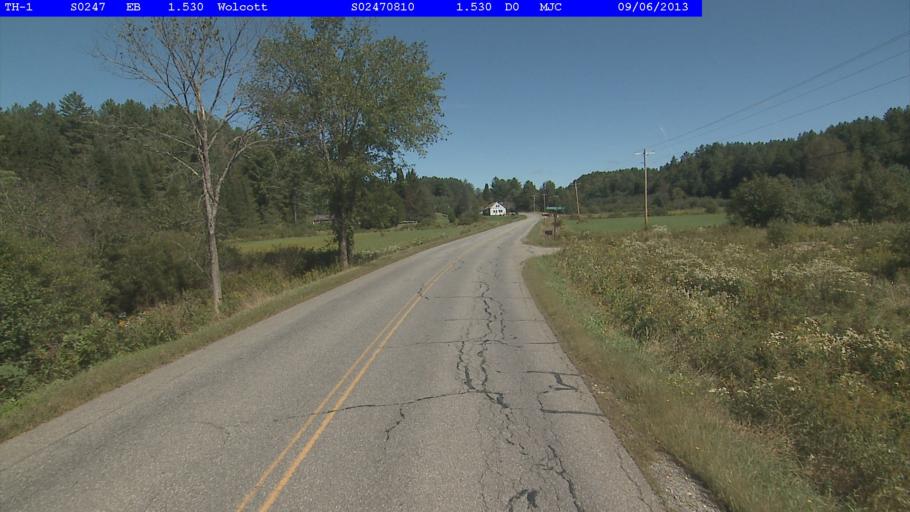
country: US
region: Vermont
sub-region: Lamoille County
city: Morrisville
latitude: 44.5779
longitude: -72.4767
